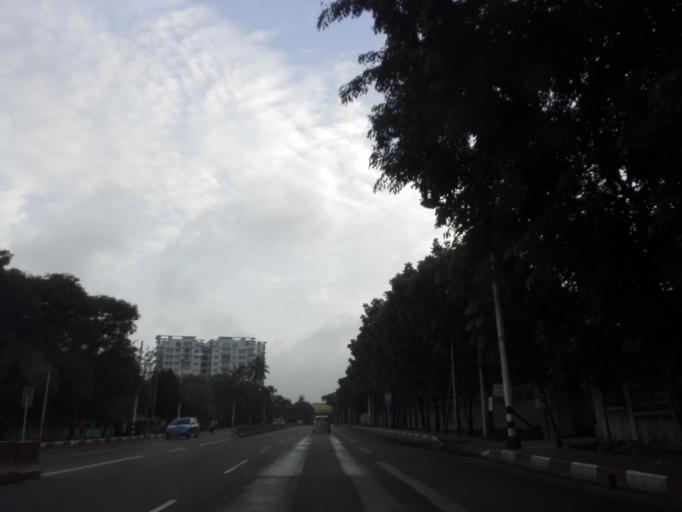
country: MM
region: Yangon
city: Yangon
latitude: 16.8453
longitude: 96.1360
